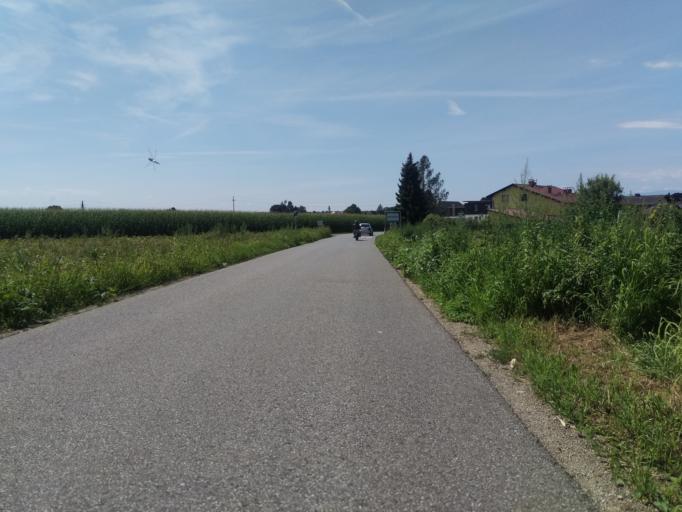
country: AT
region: Styria
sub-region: Politischer Bezirk Graz-Umgebung
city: Unterpremstatten
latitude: 46.9799
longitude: 15.4099
